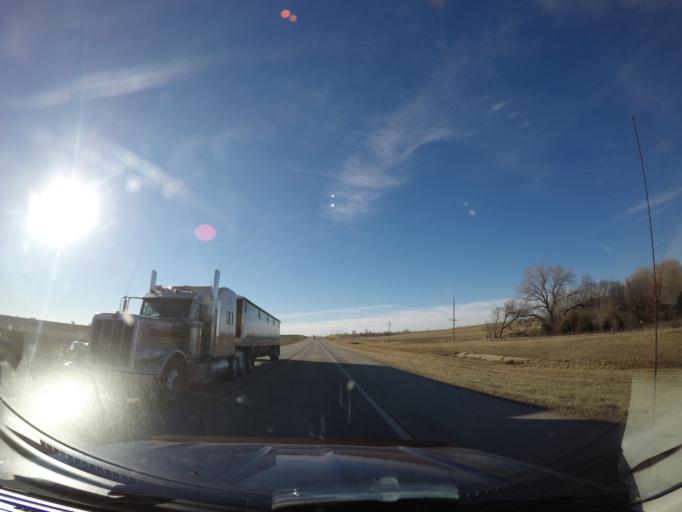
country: US
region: Kansas
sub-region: Marion County
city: Hillsboro
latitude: 38.3624
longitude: -97.3245
